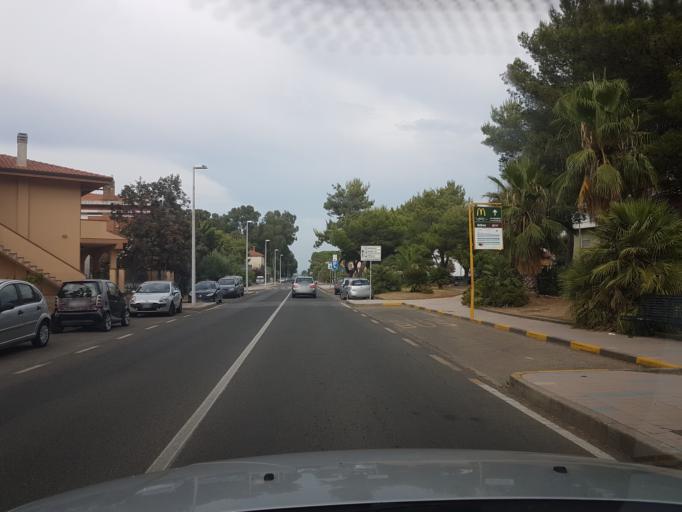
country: IT
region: Sardinia
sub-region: Provincia di Oristano
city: Cabras
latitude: 39.9070
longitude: 8.5173
